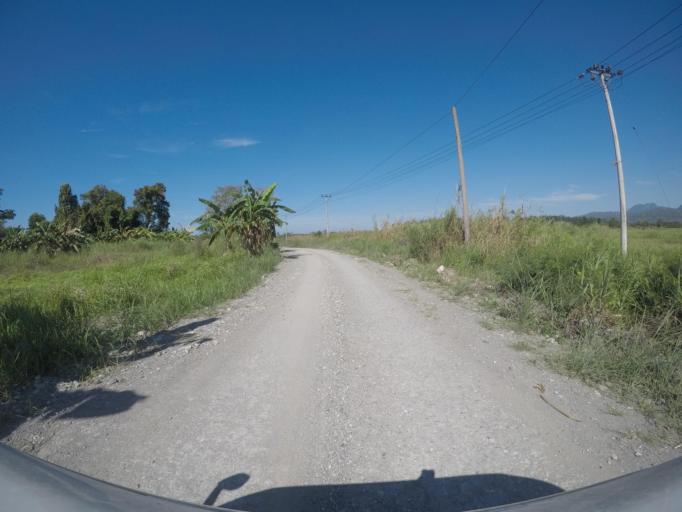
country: TL
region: Viqueque
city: Viqueque
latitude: -8.9395
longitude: 126.1153
